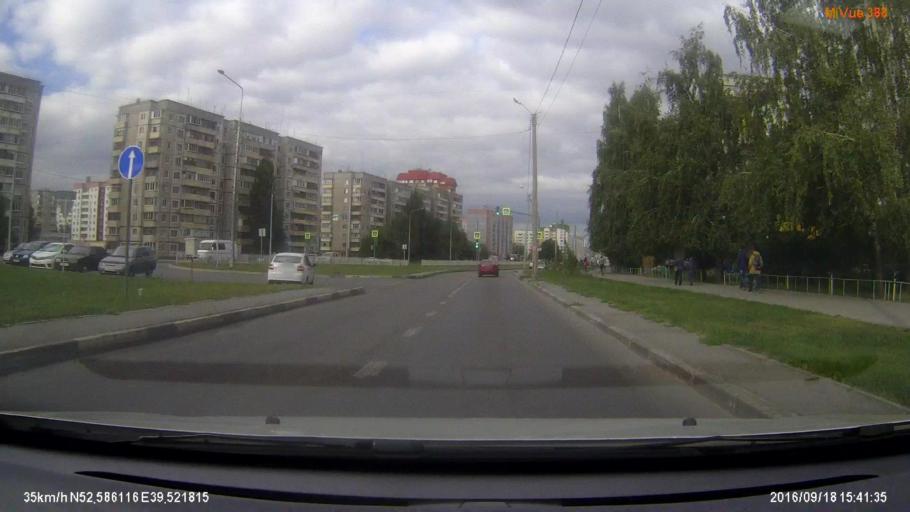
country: RU
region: Lipetsk
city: Syrskoye
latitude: 52.5864
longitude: 39.5226
